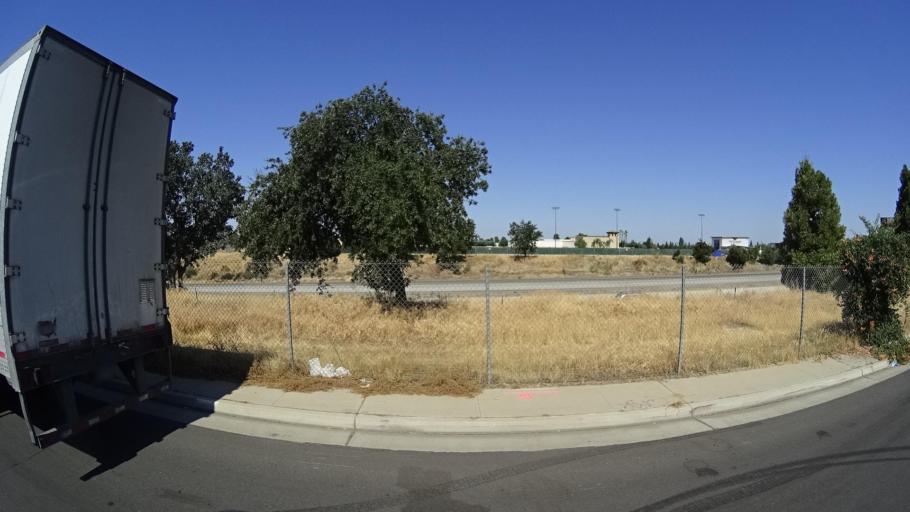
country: US
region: California
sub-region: Fresno County
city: Fresno
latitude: 36.7885
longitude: -119.7483
